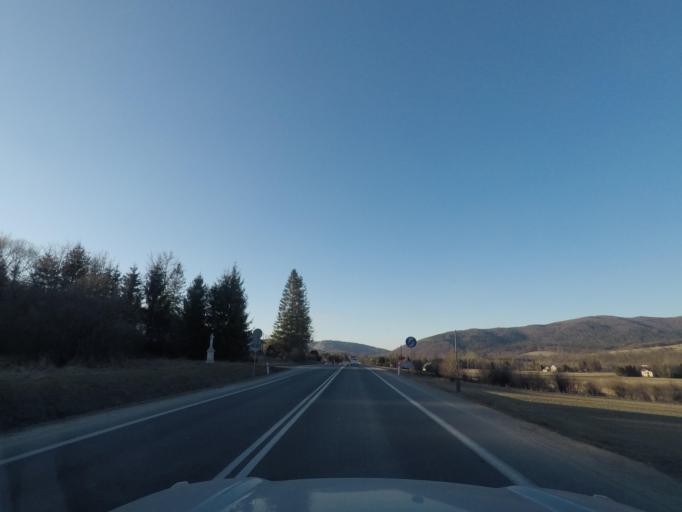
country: PL
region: Subcarpathian Voivodeship
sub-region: Powiat krosnienski
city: Dukla
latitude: 49.4975
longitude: 21.7010
